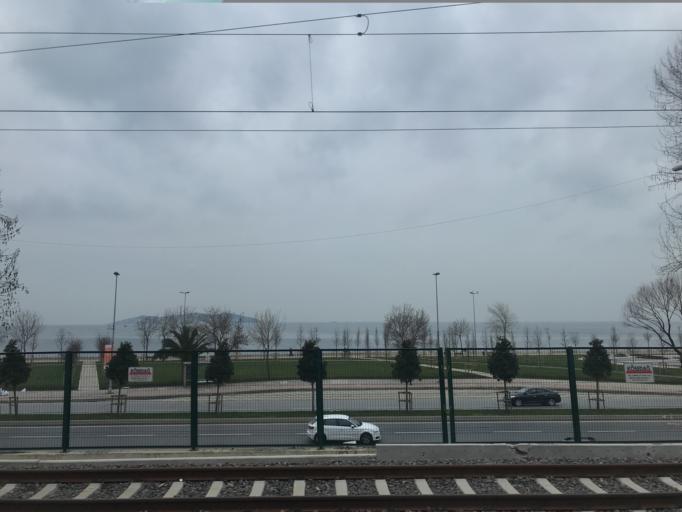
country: TR
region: Istanbul
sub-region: Atasehir
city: Atasehir
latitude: 40.9491
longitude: 29.1009
